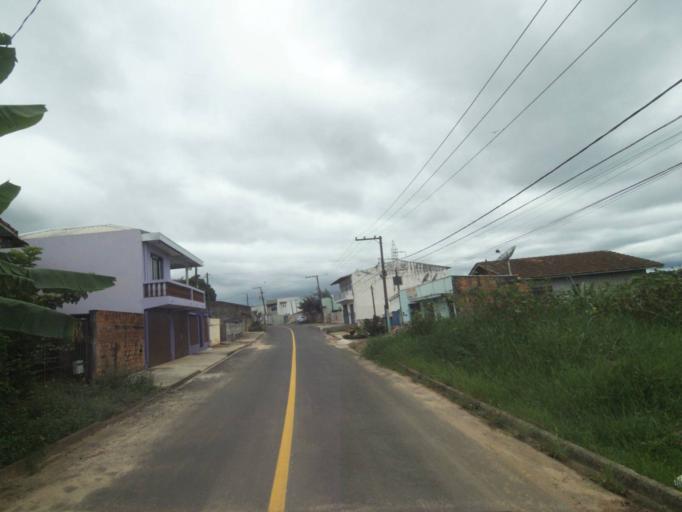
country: BR
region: Parana
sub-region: Telemaco Borba
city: Telemaco Borba
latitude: -24.3333
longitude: -50.6074
